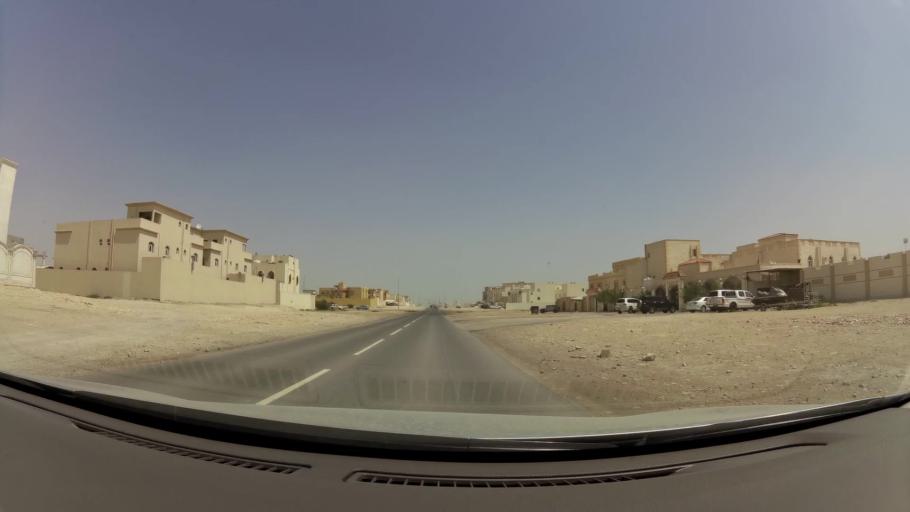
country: QA
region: Baladiyat Umm Salal
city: Umm Salal Muhammad
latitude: 25.4018
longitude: 51.4477
